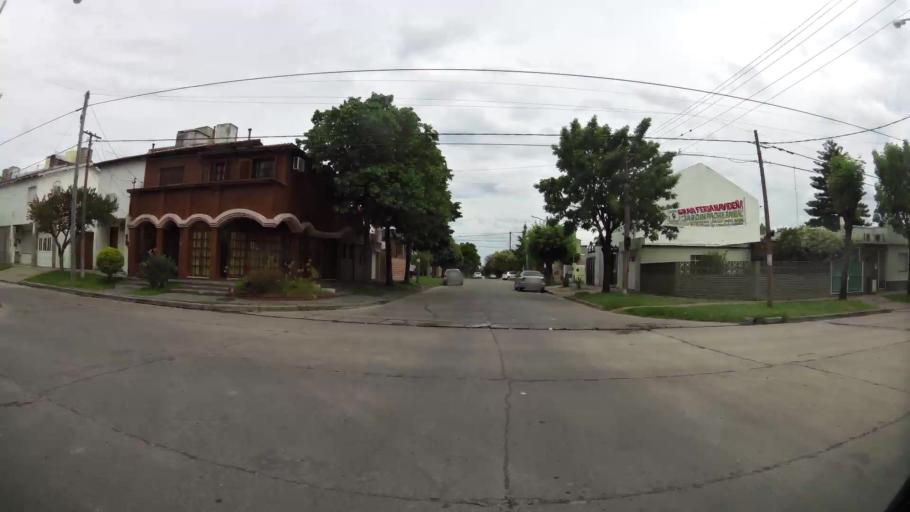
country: AR
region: Buenos Aires
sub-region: Partido de Campana
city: Campana
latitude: -34.1750
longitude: -58.9694
